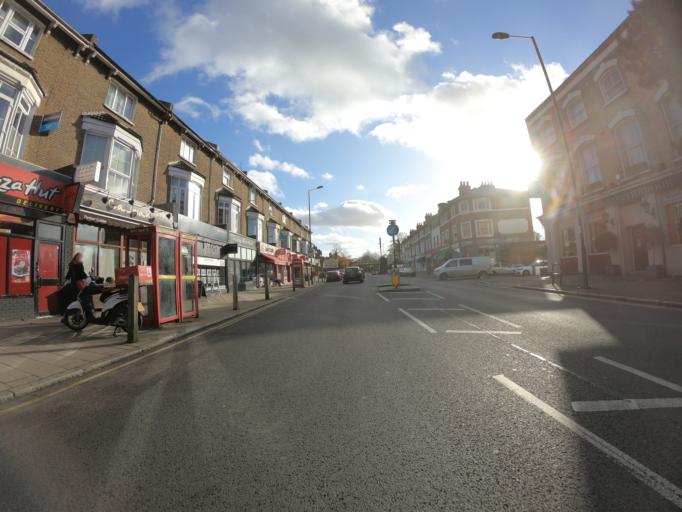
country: GB
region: England
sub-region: Greater London
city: Blackheath
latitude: 51.4510
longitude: 0.0125
